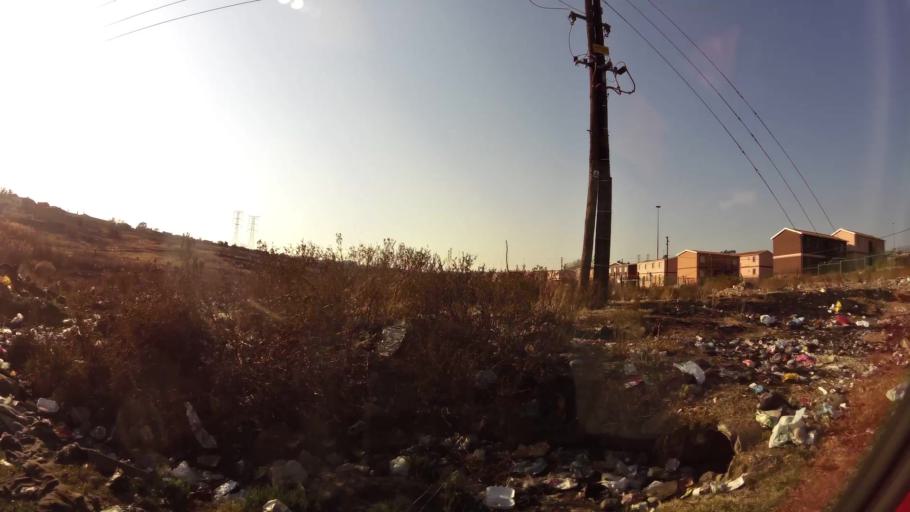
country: ZA
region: Gauteng
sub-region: City of Johannesburg Metropolitan Municipality
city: Soweto
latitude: -26.2568
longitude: 27.9520
